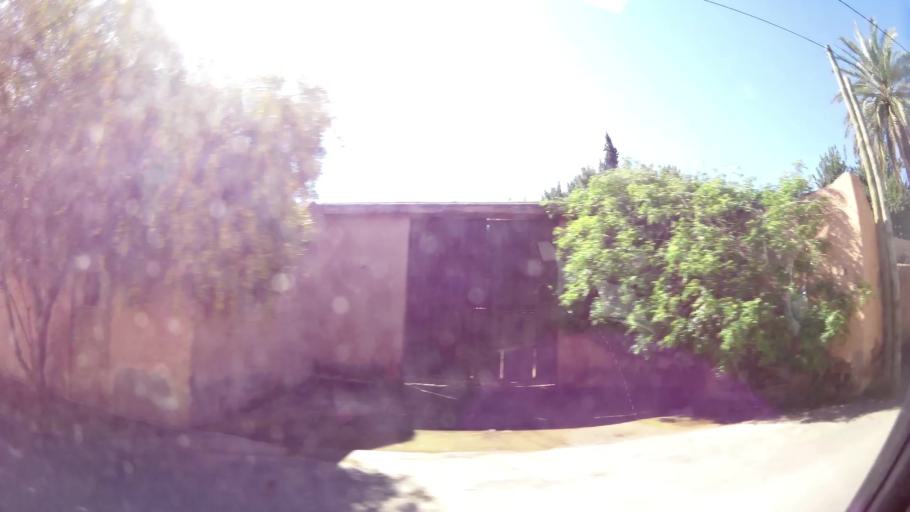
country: MA
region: Marrakech-Tensift-Al Haouz
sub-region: Marrakech
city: Marrakesh
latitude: 31.6678
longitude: -7.9646
